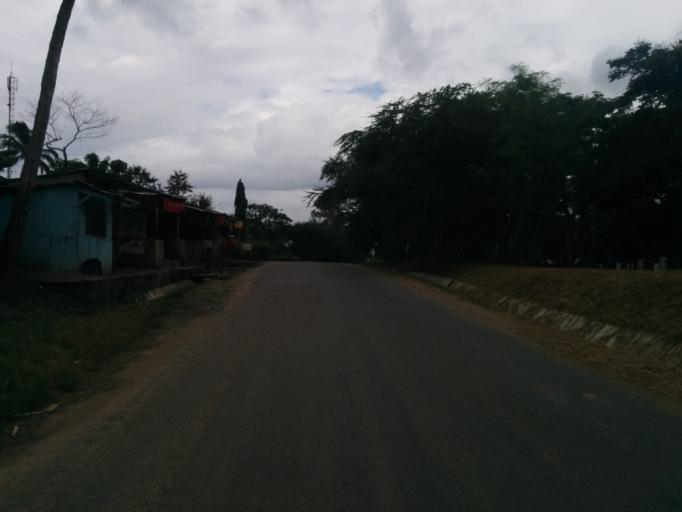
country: TZ
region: Dar es Salaam
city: Magomeni
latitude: -6.7700
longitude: 39.1955
